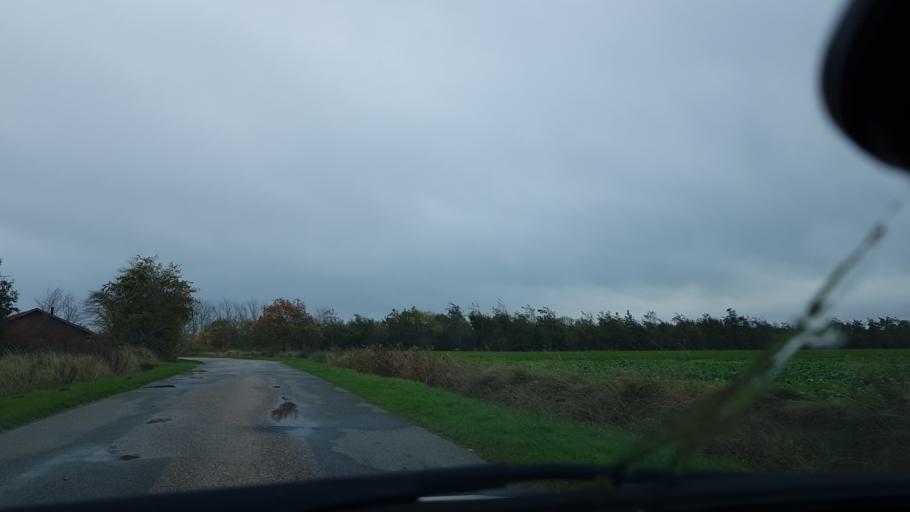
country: DK
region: South Denmark
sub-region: Tonder Kommune
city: Sherrebek
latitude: 55.2139
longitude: 8.8006
